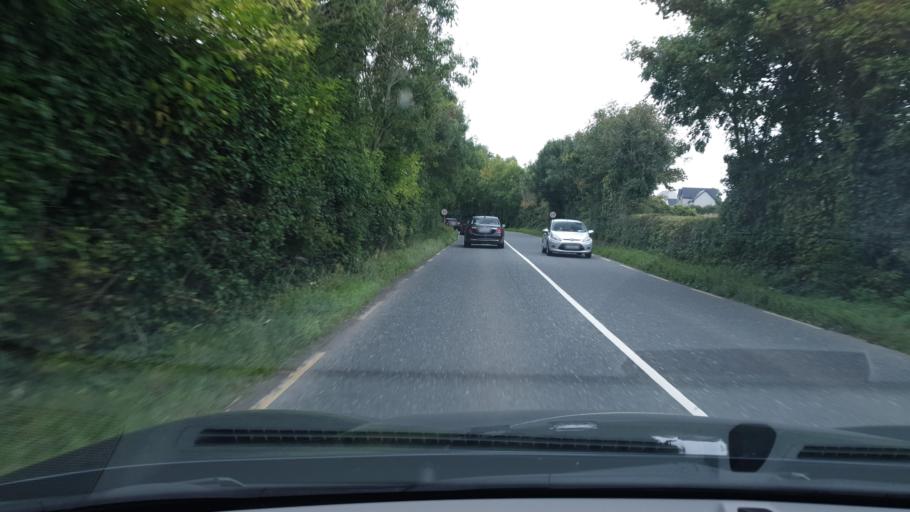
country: IE
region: Leinster
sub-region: An Mhi
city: Dunshaughlin
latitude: 53.5180
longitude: -6.5337
